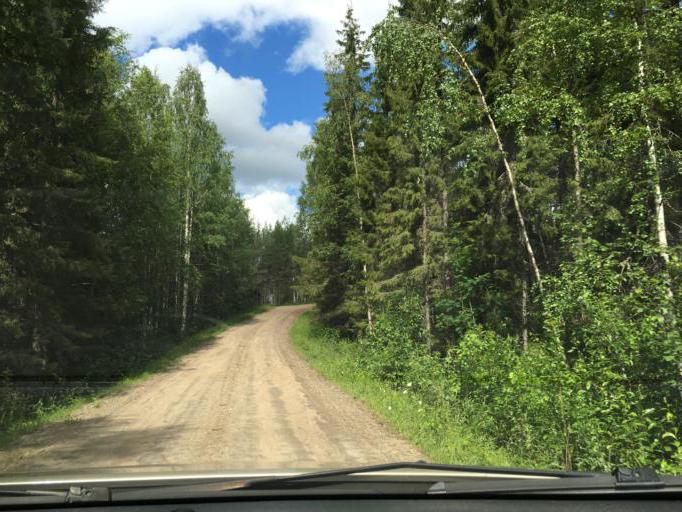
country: SE
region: Norrbotten
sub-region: Overkalix Kommun
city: OEverkalix
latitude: 66.1326
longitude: 22.7840
